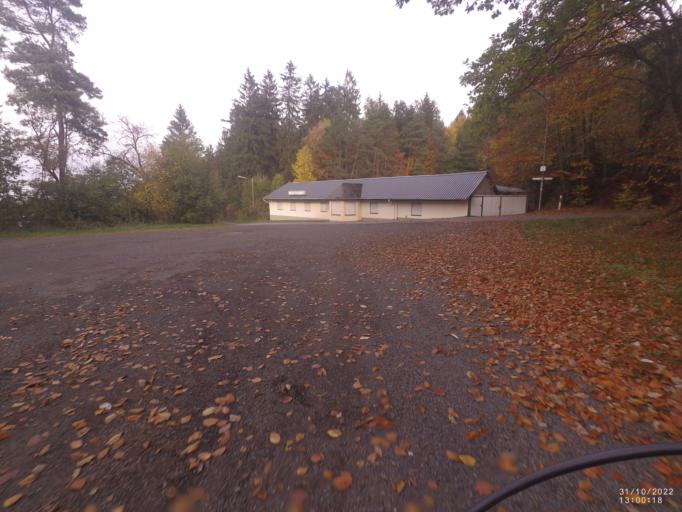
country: DE
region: Rheinland-Pfalz
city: Kelberg
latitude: 50.2784
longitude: 6.9190
